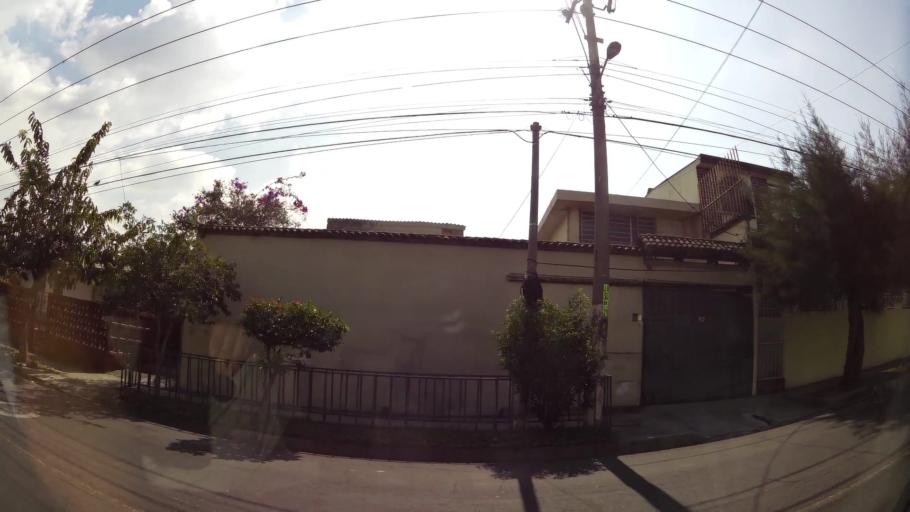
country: SV
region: San Salvador
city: Mejicanos
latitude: 13.7223
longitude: -89.2109
